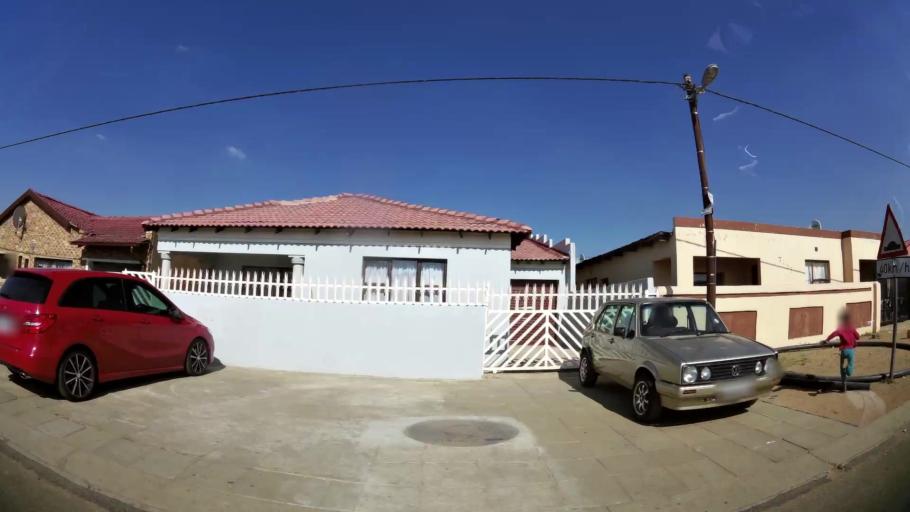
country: ZA
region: Gauteng
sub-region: City of Johannesburg Metropolitan Municipality
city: Roodepoort
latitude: -26.1605
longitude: 27.7987
